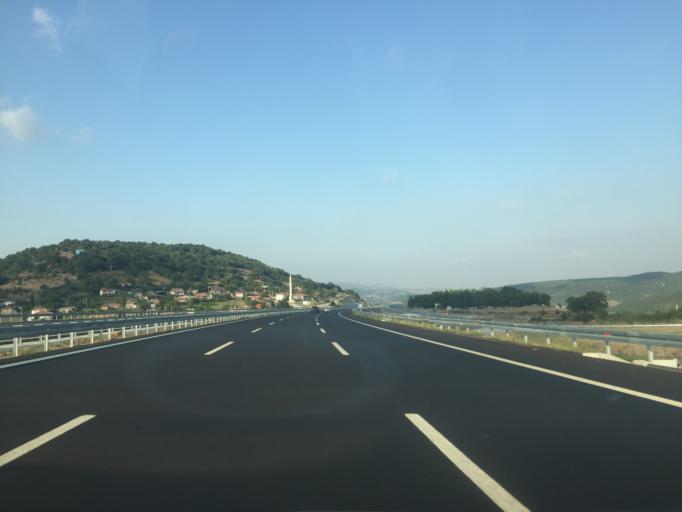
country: TR
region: Balikesir
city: Ertugrul
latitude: 39.5485
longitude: 27.6835
